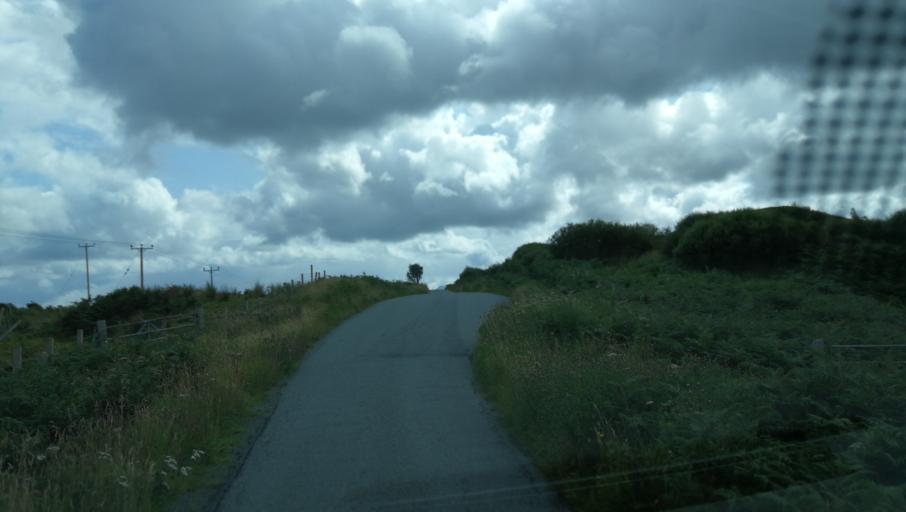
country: GB
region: Scotland
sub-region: Highland
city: Portree
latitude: 57.3804
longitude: -6.1713
